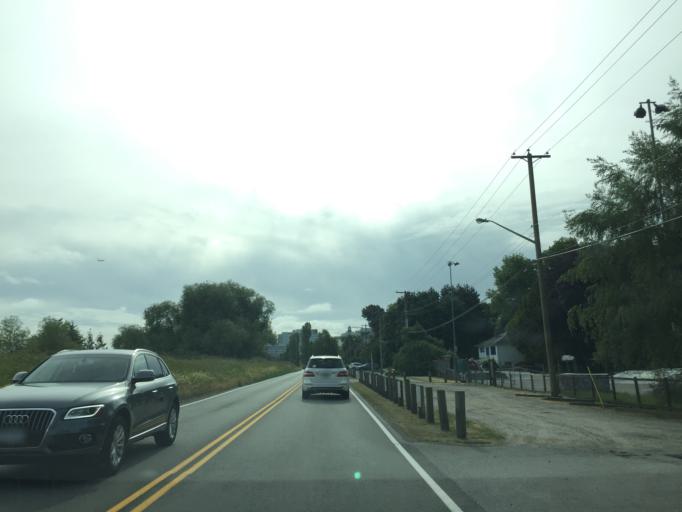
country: CA
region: British Columbia
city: Richmond
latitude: 49.1735
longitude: -123.1674
